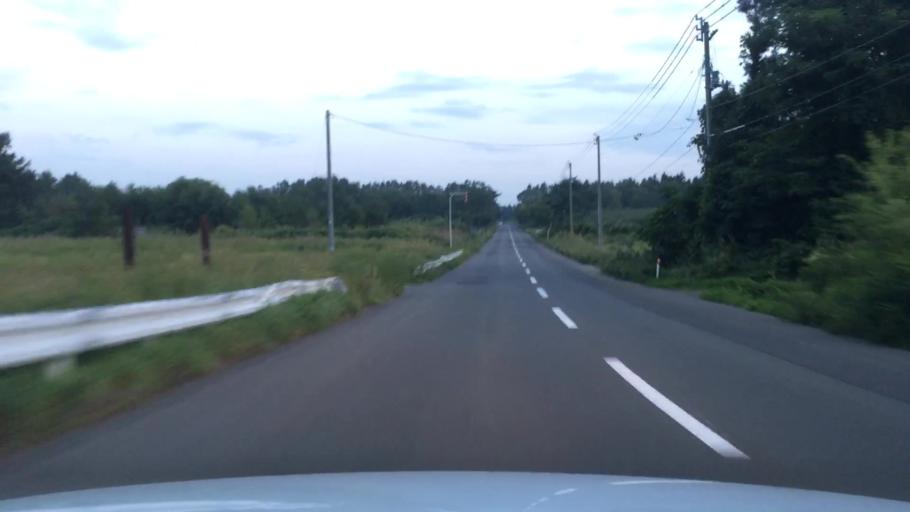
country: JP
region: Aomori
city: Shimokizukuri
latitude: 40.6854
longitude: 140.3693
